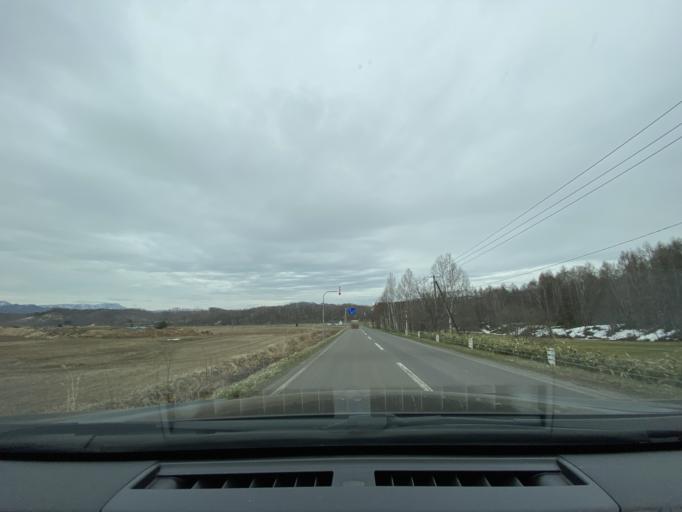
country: JP
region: Hokkaido
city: Nayoro
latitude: 44.0926
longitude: 142.4696
